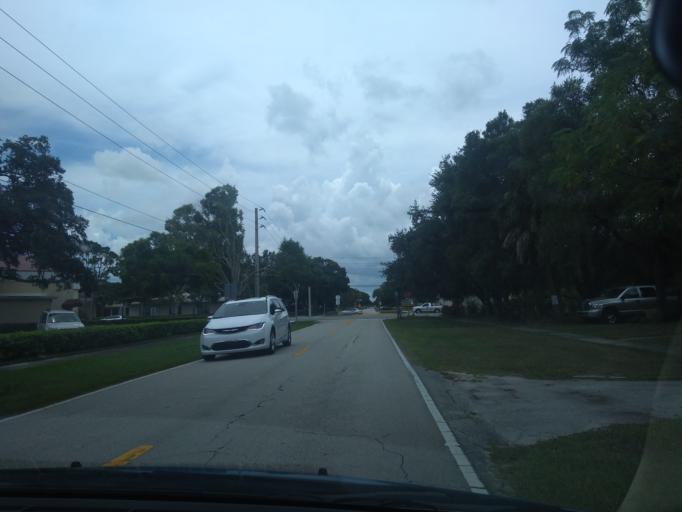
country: US
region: Florida
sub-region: Indian River County
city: Vero Beach
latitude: 27.6392
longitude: -80.4205
